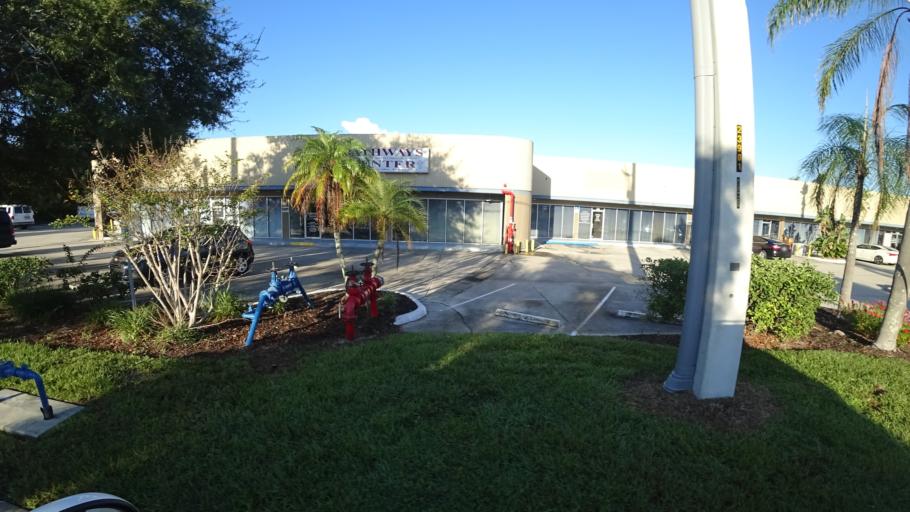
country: US
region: Florida
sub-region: Manatee County
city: Bradenton
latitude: 27.4930
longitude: -82.5655
